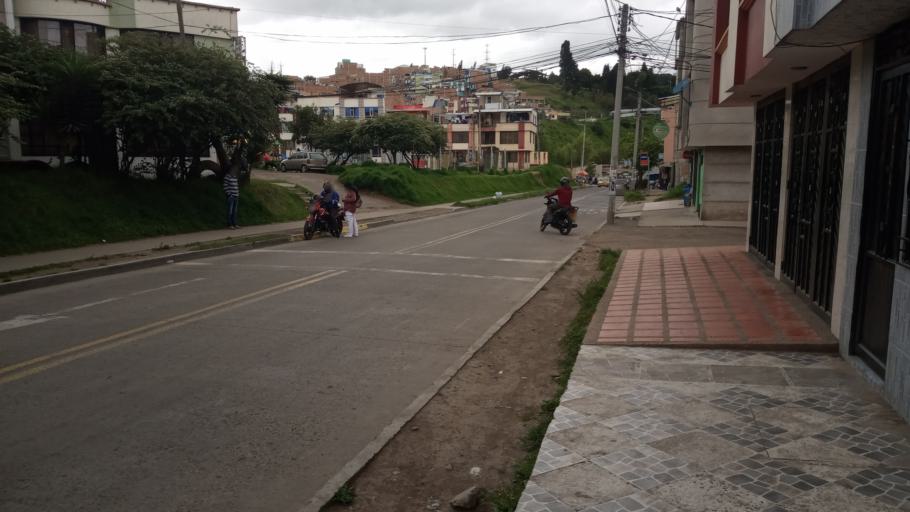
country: CO
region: Narino
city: Pasto
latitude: 1.1978
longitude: -77.2848
